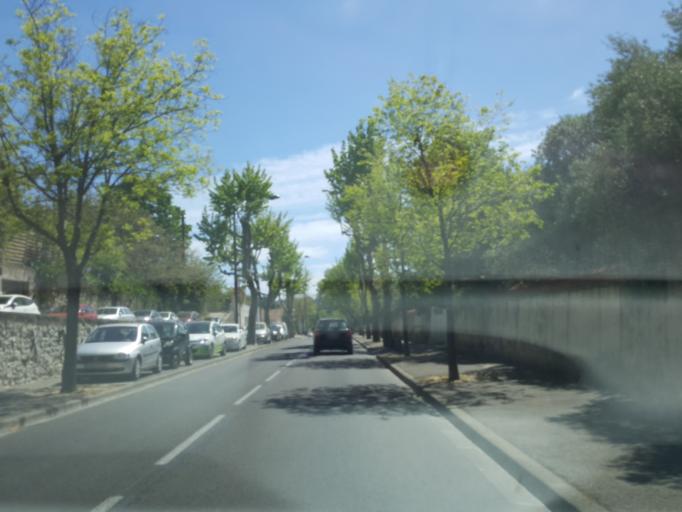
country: FR
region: Provence-Alpes-Cote d'Azur
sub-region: Departement des Bouches-du-Rhone
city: Roquevaire
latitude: 43.3472
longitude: 5.6035
